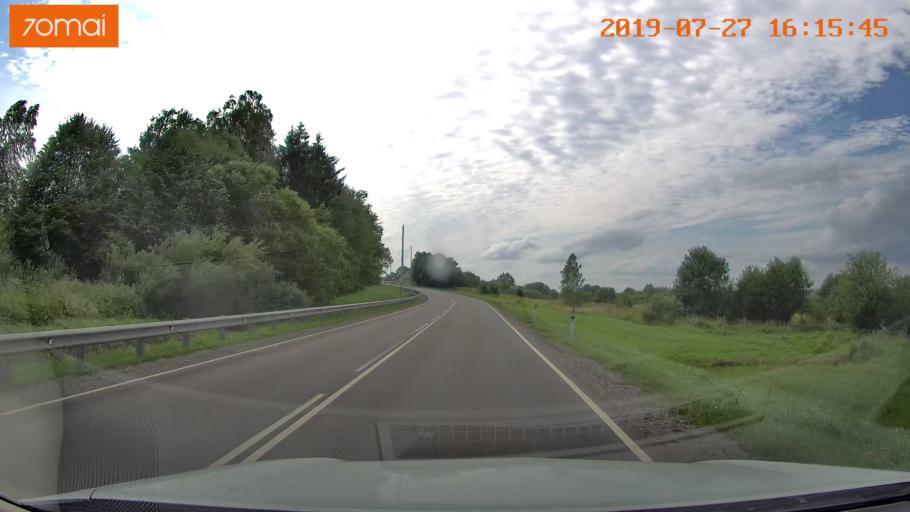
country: RU
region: Kaliningrad
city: Chernyakhovsk
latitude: 54.6250
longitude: 21.5877
